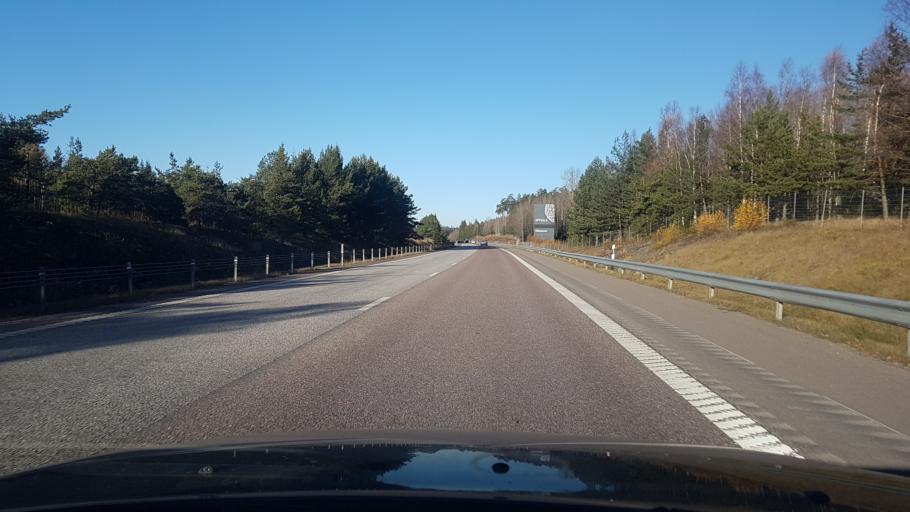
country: SE
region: Uppsala
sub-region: Uppsala Kommun
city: Alsike
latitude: 59.7698
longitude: 17.7885
